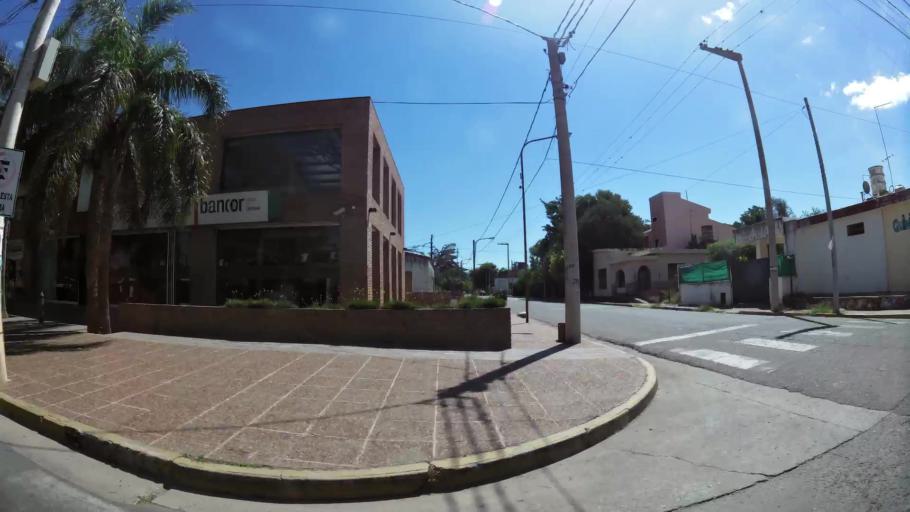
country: AR
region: Cordoba
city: Villa Allende
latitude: -31.2923
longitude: -64.2977
